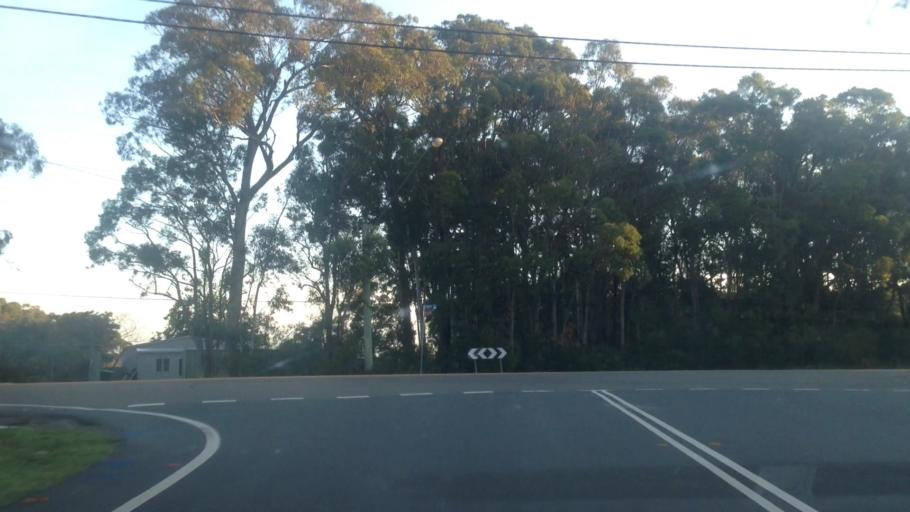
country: AU
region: New South Wales
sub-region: Wyong Shire
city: Kingfisher Shores
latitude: -33.1524
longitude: 151.5187
